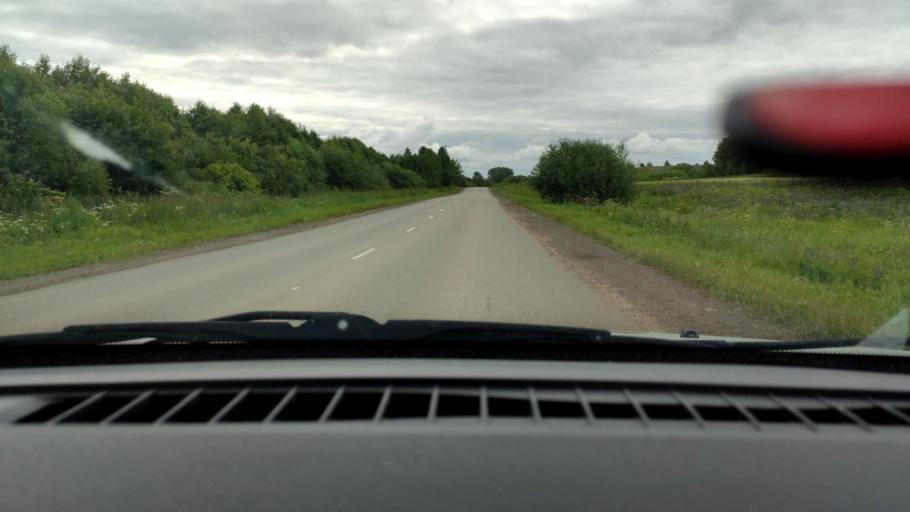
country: RU
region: Perm
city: Chaykovskaya
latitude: 58.1208
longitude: 55.5689
